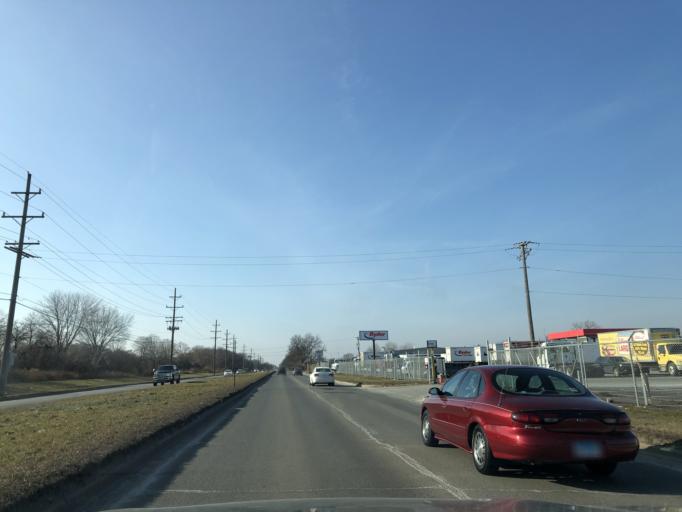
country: US
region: Illinois
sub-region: Cook County
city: Cicero
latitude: 41.8219
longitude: -87.7552
